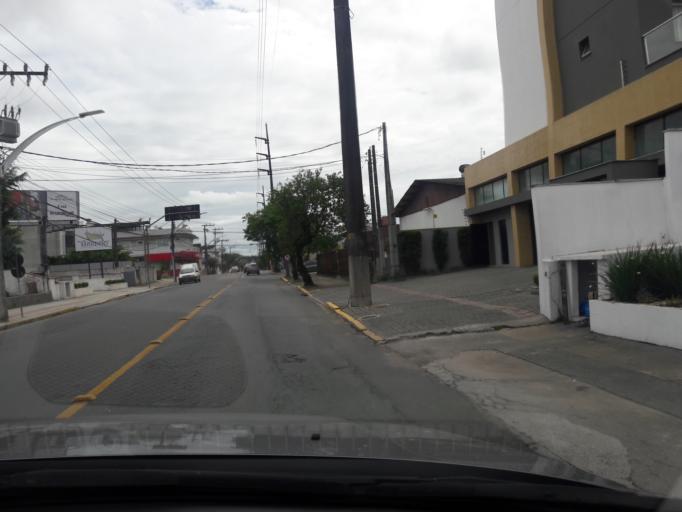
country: BR
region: Santa Catarina
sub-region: Joinville
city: Joinville
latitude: -26.3170
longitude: -48.8484
